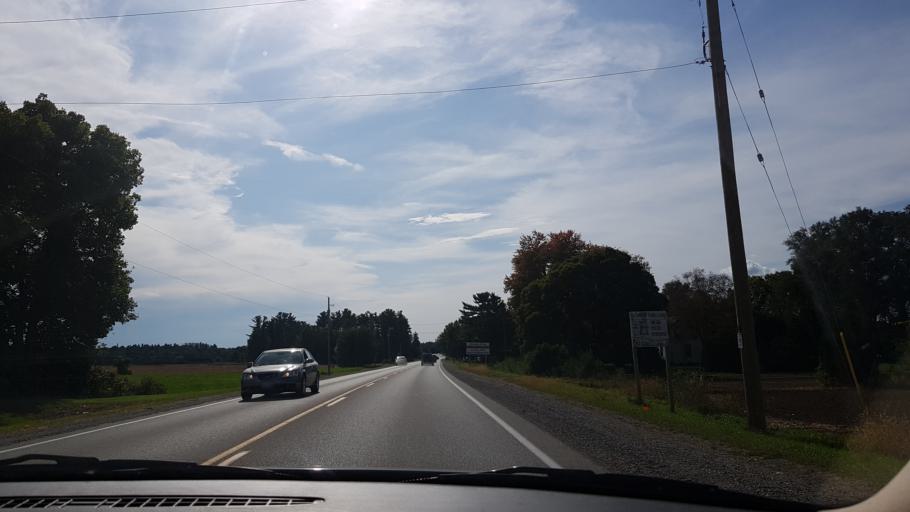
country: CA
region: Ontario
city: Delaware
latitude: 42.9276
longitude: -81.4545
